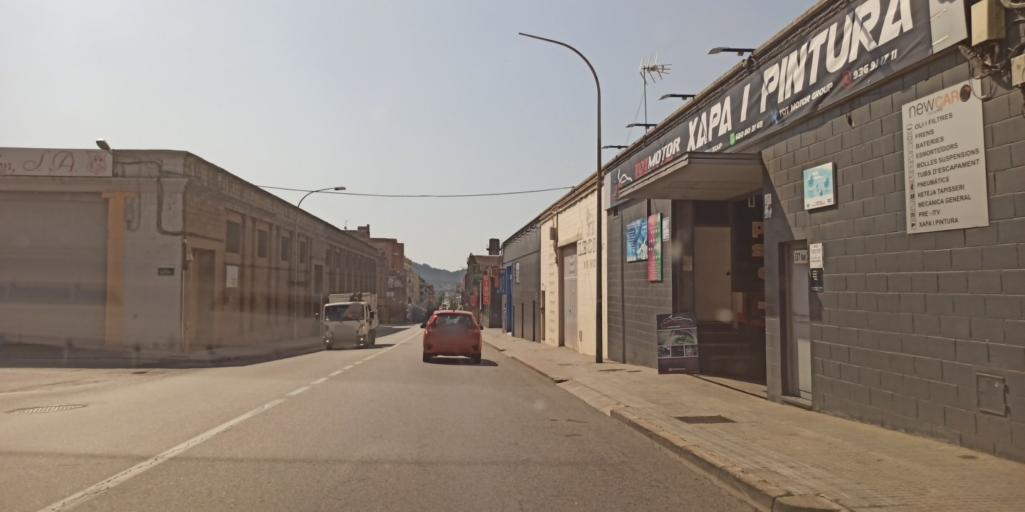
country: ES
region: Catalonia
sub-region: Provincia de Barcelona
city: Cerdanyola del Valles
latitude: 41.4965
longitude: 2.1437
